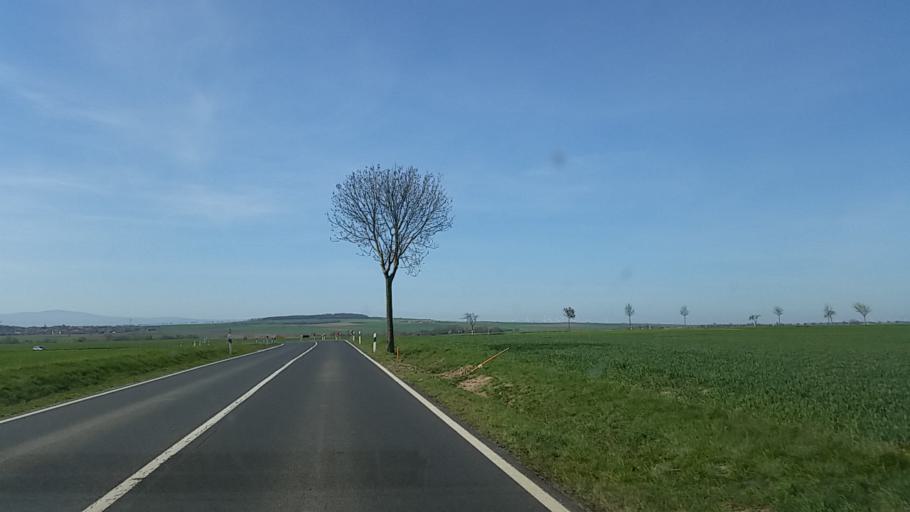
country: DE
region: Lower Saxony
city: Twieflingen
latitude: 52.1137
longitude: 10.9297
